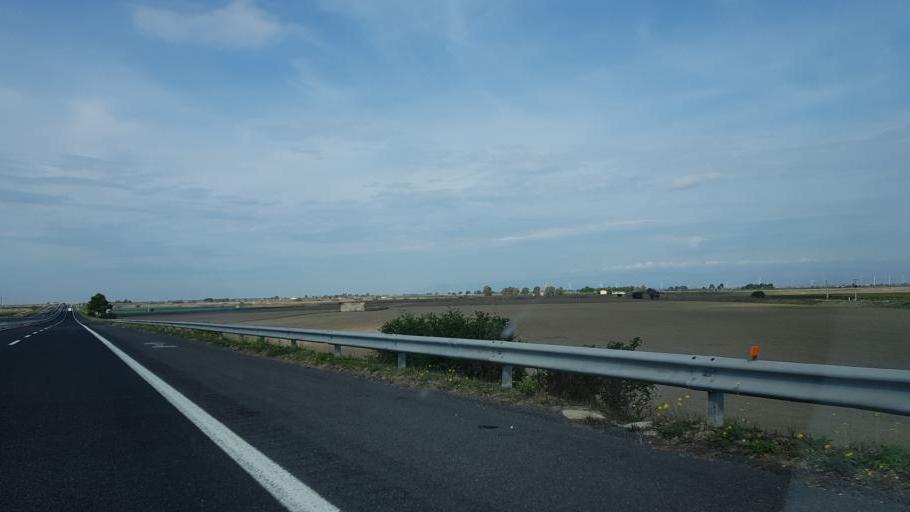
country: IT
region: Apulia
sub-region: Provincia di Foggia
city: Orta Nova
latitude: 41.3733
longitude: 15.7660
